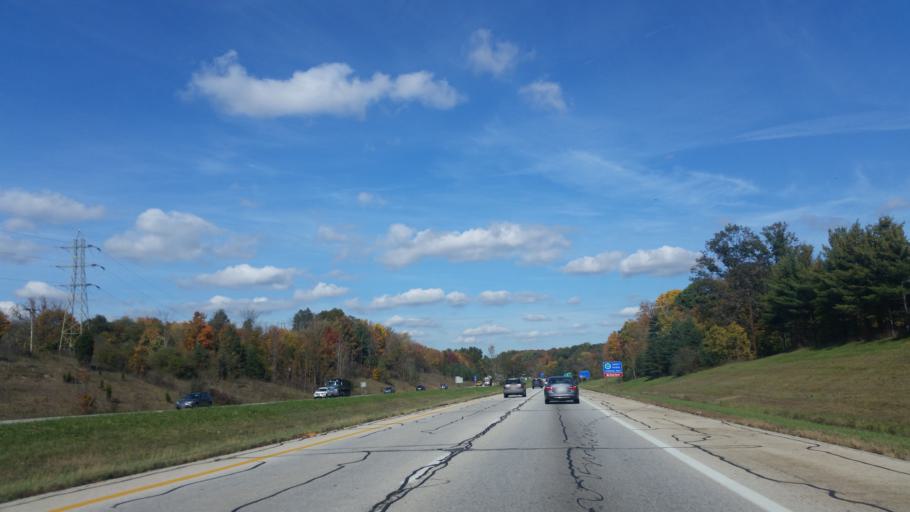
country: US
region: Ohio
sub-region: Summit County
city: Richfield
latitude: 41.2436
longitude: -81.6286
